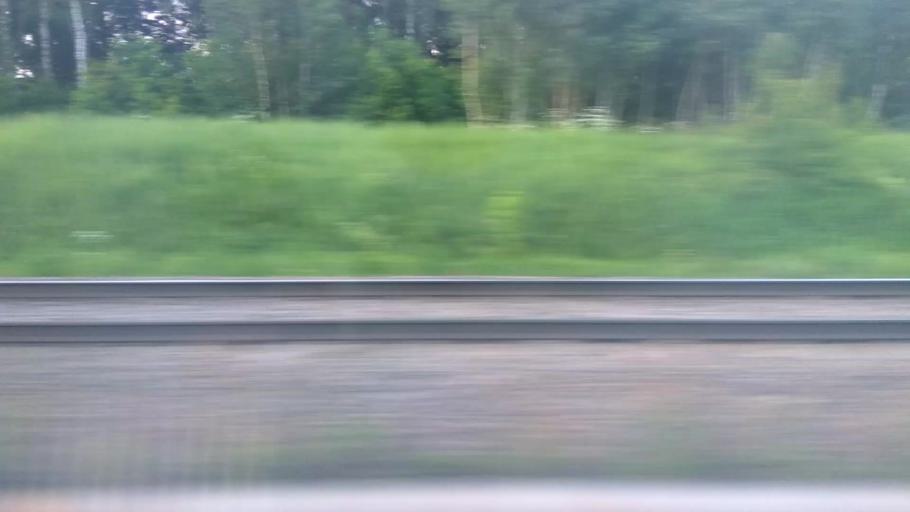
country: RU
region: Moskovskaya
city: Vostryakovo
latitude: 55.3802
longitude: 37.8162
